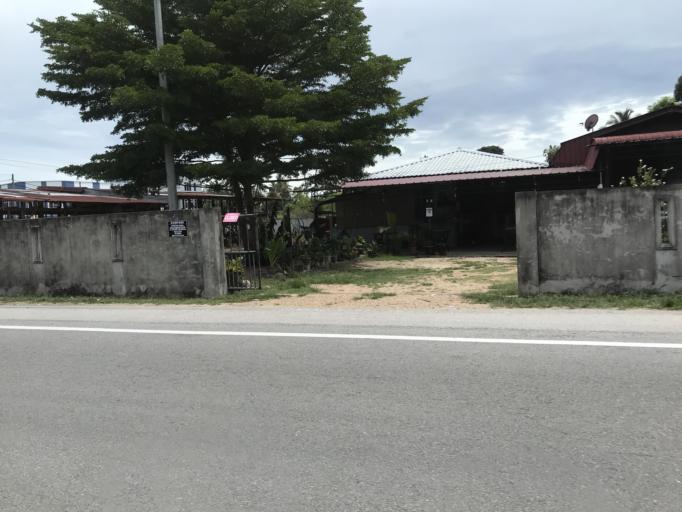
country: MY
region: Kelantan
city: Tumpat
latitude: 6.1775
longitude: 102.1801
